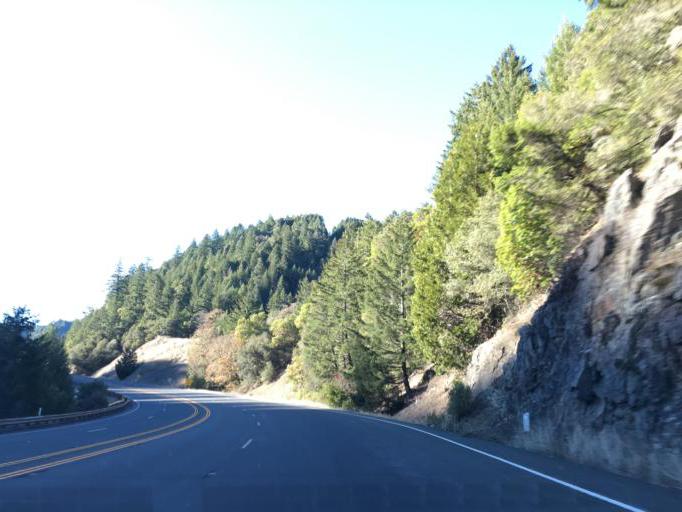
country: US
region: California
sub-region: Mendocino County
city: Laytonville
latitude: 39.8323
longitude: -123.6197
